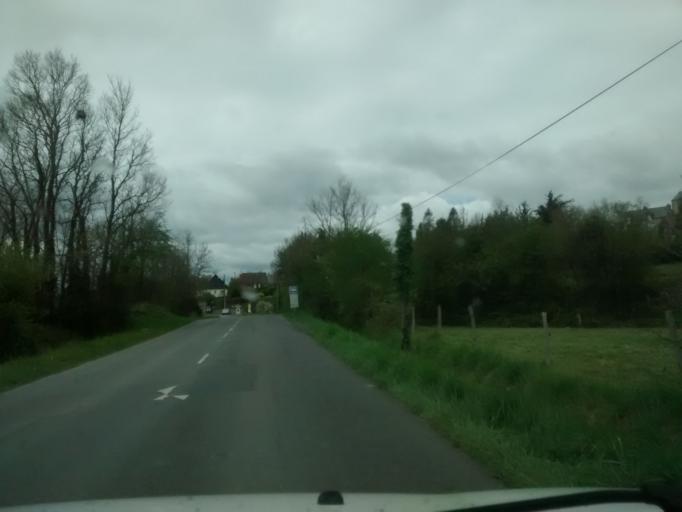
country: FR
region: Brittany
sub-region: Departement d'Ille-et-Vilaine
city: Saint-Jouan-des-Guerets
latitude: 48.5743
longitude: -1.9607
